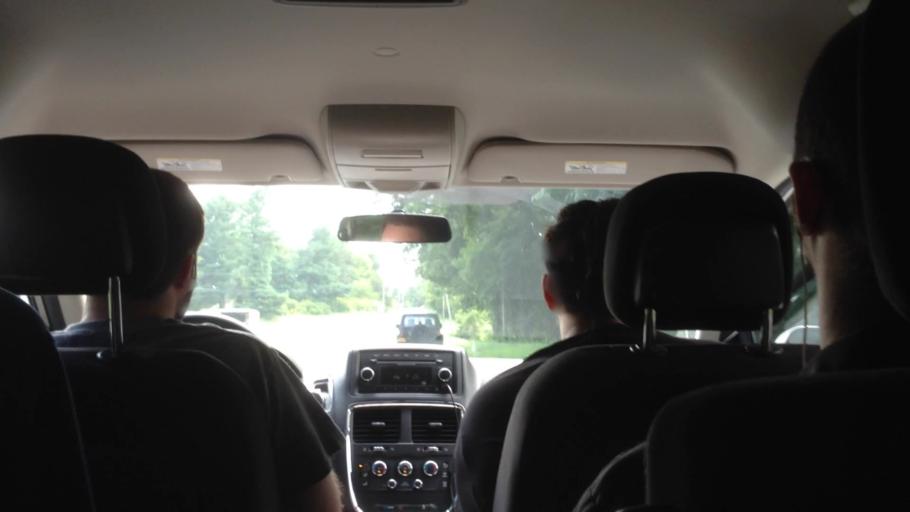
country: US
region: New York
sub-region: Dutchess County
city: Tivoli
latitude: 42.0805
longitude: -73.8956
